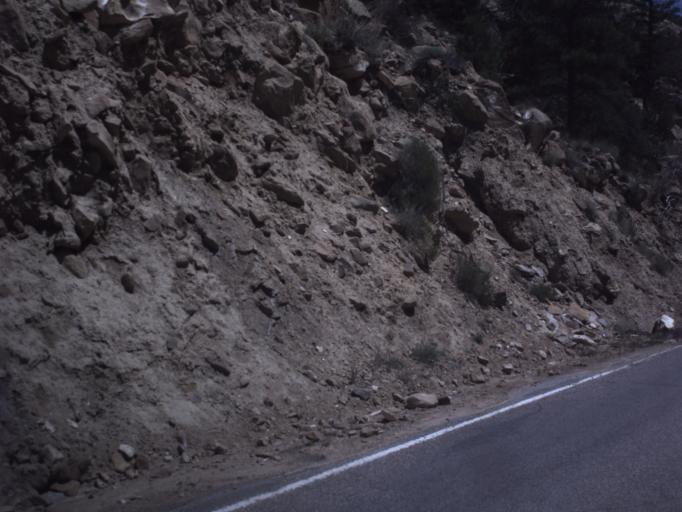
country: US
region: Utah
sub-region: Emery County
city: Orangeville
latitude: 39.2859
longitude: -111.2378
